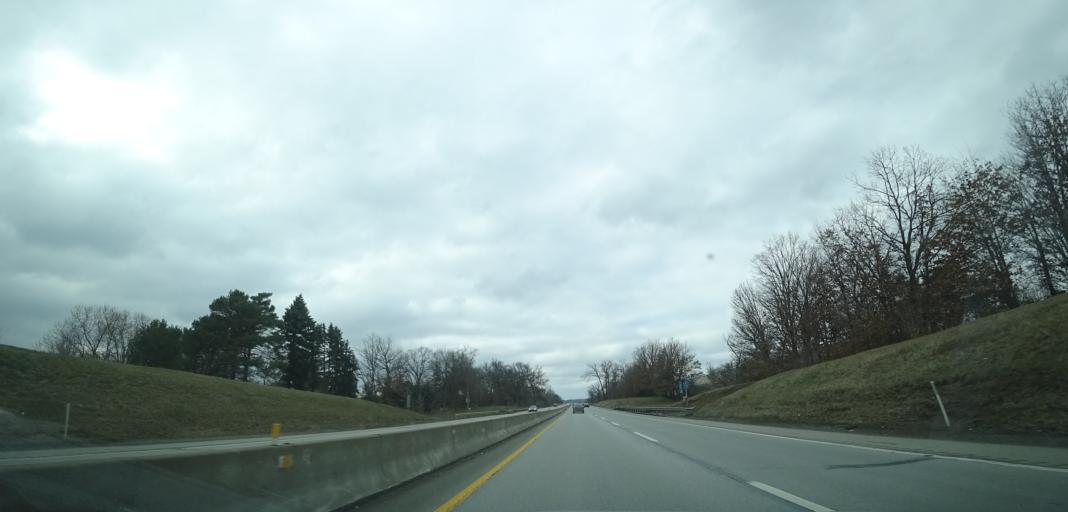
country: US
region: Pennsylvania
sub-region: Butler County
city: Cranberry Township
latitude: 40.6869
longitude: -80.1095
